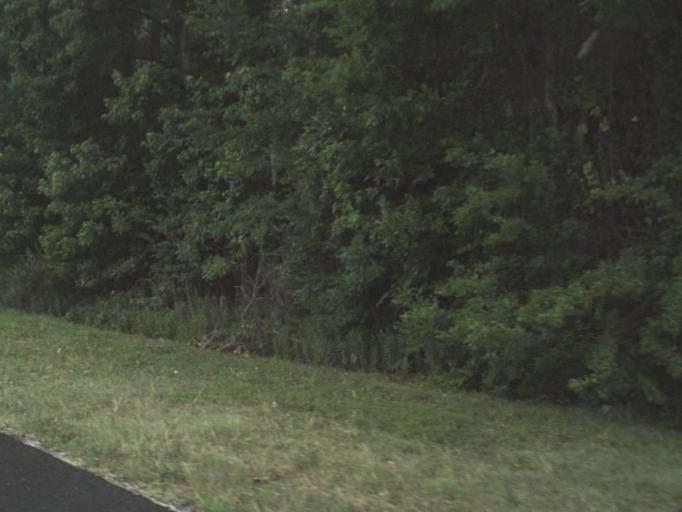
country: US
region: Florida
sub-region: Marion County
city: Citra
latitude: 29.3048
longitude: -82.1519
